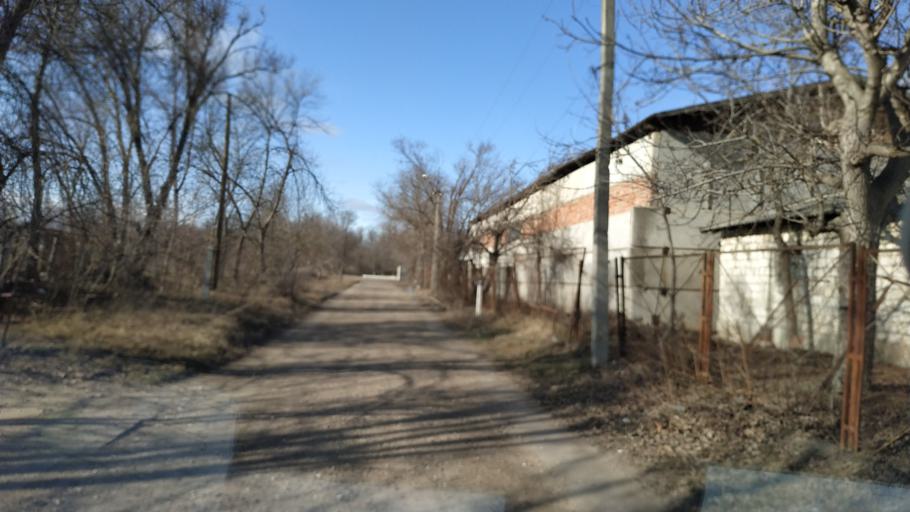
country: MD
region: Causeni
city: Causeni
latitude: 46.6613
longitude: 29.4223
